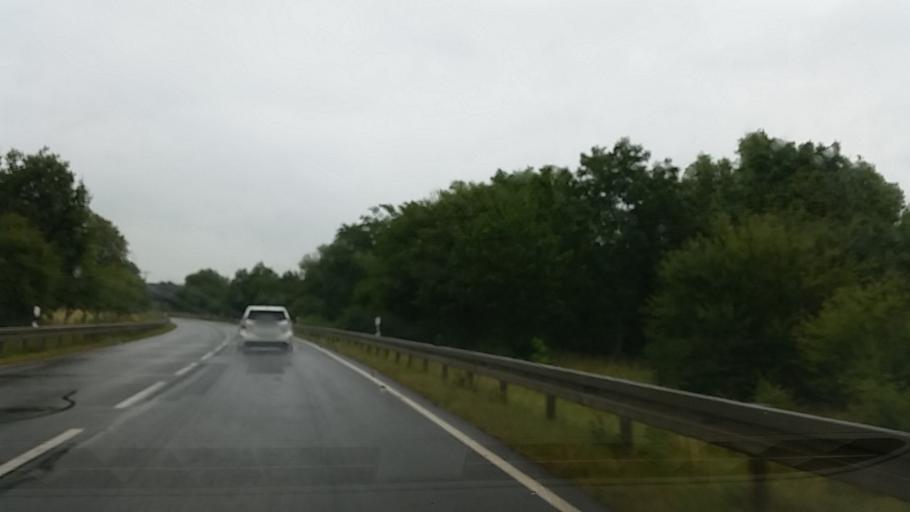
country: DE
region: Mecklenburg-Vorpommern
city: Kropelin
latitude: 54.0706
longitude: 11.7828
